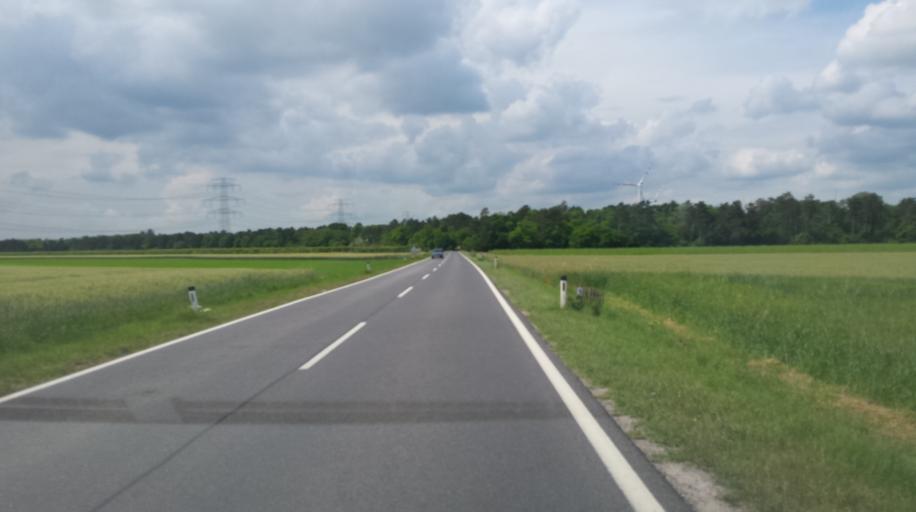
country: AT
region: Lower Austria
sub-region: Politischer Bezirk Ganserndorf
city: Deutsch-Wagram
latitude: 48.3015
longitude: 16.5466
